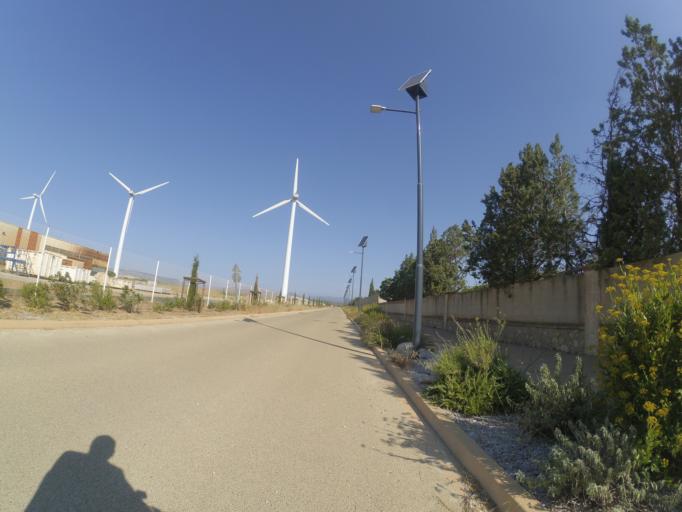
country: FR
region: Languedoc-Roussillon
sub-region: Departement des Pyrenees-Orientales
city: Salses-le-Chateau
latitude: 42.8042
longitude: 2.8930
